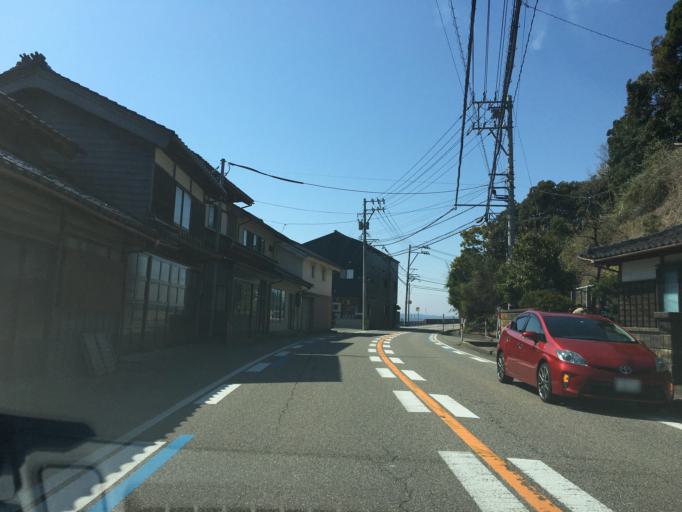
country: JP
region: Toyama
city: Himi
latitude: 36.8949
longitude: 137.0064
